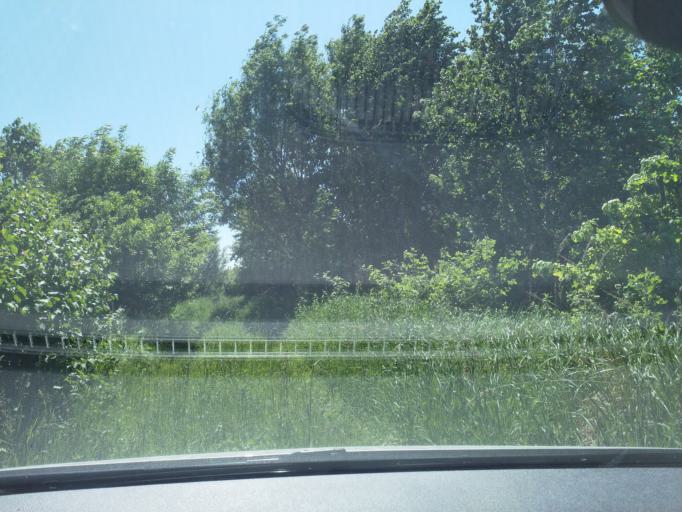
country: LV
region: Kuldigas Rajons
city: Kuldiga
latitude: 56.9771
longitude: 21.9463
